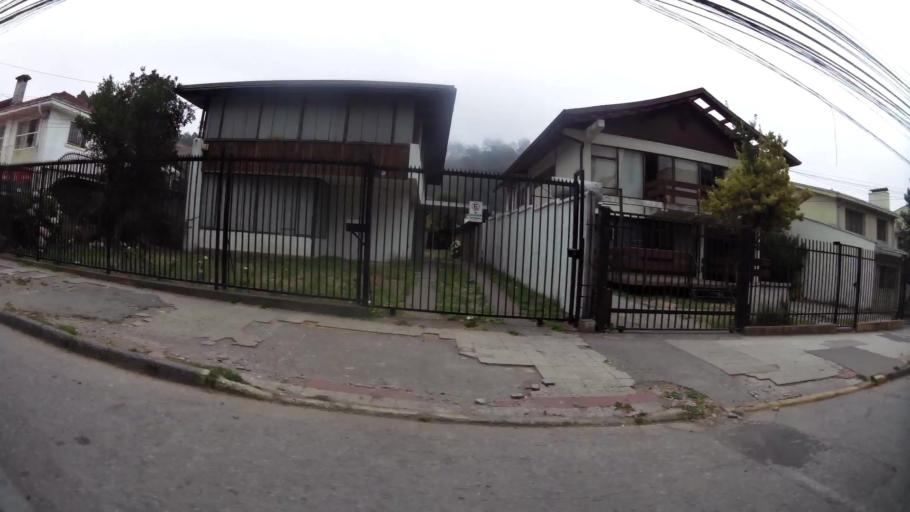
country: CL
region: Biobio
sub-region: Provincia de Concepcion
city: Concepcion
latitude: -36.8312
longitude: -73.0373
